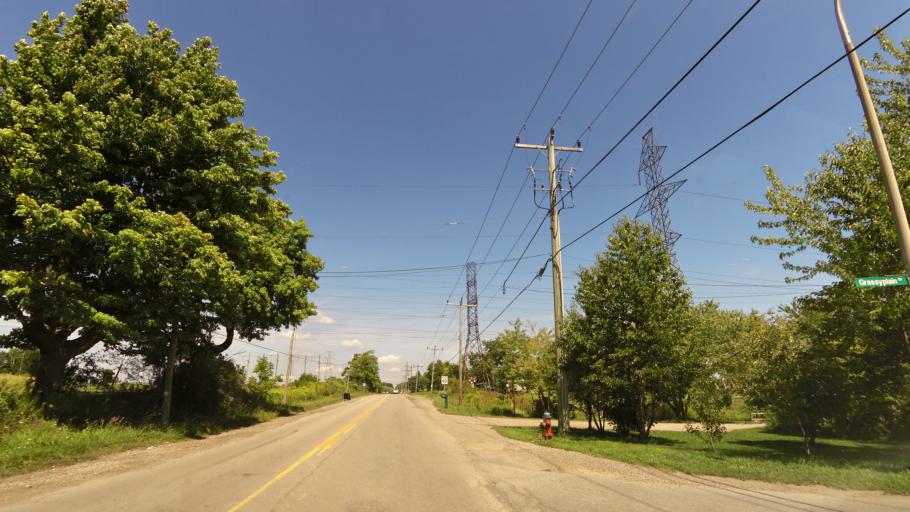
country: CA
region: Ontario
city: Ancaster
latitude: 43.2035
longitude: -79.9305
